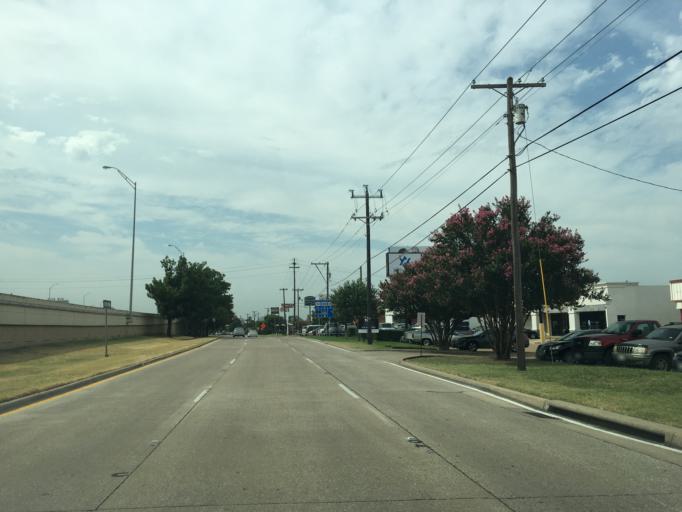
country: US
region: Texas
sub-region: Collin County
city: Plano
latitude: 33.0228
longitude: -96.7104
